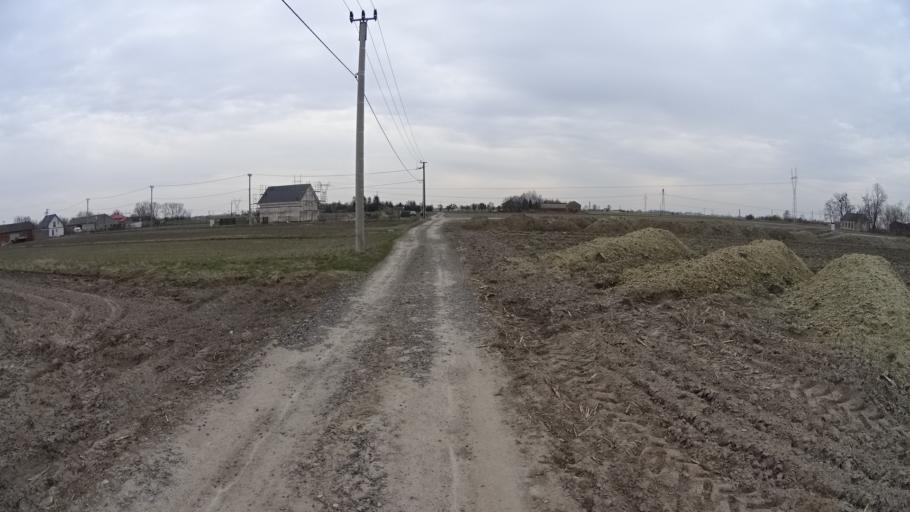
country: PL
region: Masovian Voivodeship
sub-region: Powiat warszawski zachodni
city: Jozefow
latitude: 52.2422
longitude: 20.6887
